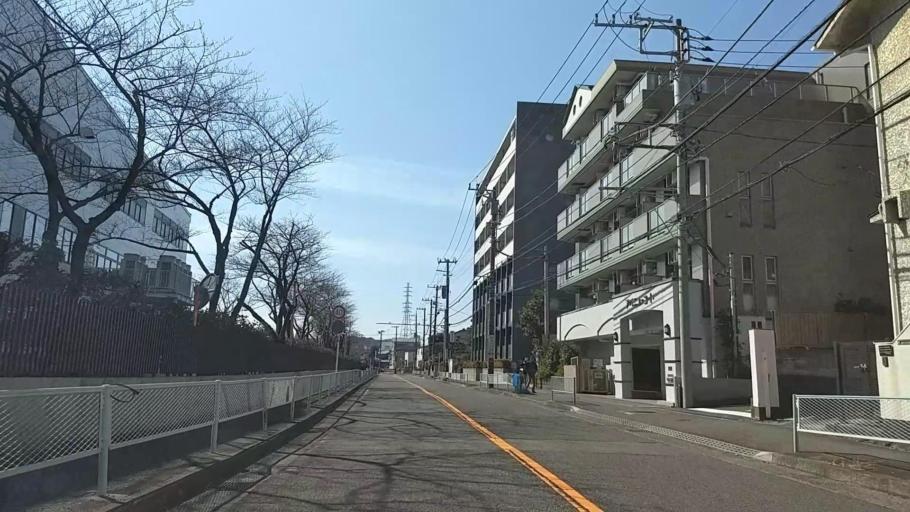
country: JP
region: Kanagawa
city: Kamakura
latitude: 35.3507
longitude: 139.5364
